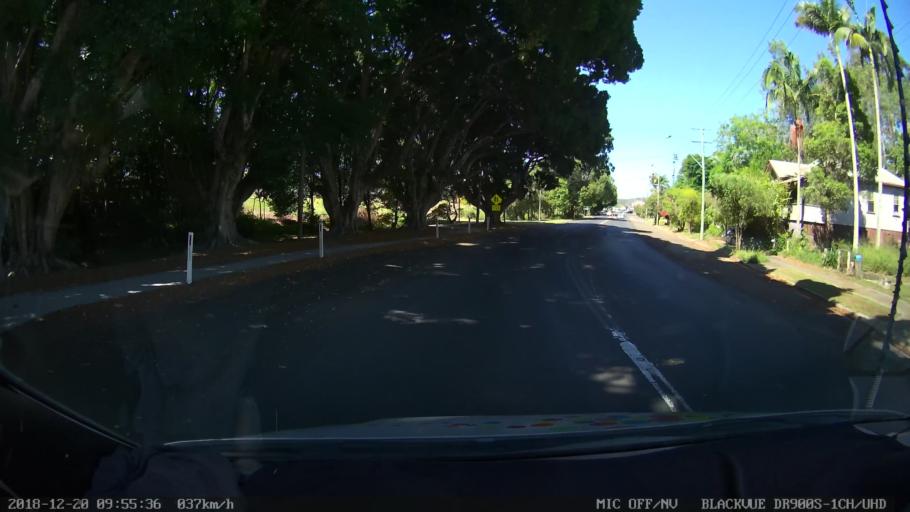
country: AU
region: New South Wales
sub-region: Lismore Municipality
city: Lismore
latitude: -28.8070
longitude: 153.2730
